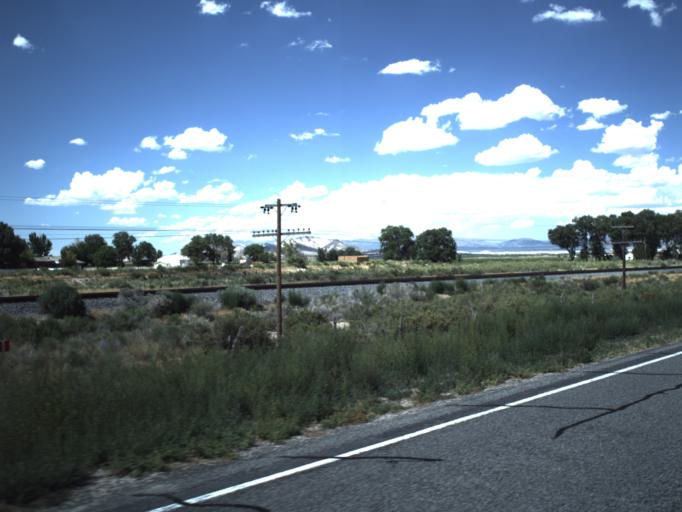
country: US
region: Utah
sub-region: Millard County
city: Delta
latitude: 39.5357
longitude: -112.3662
